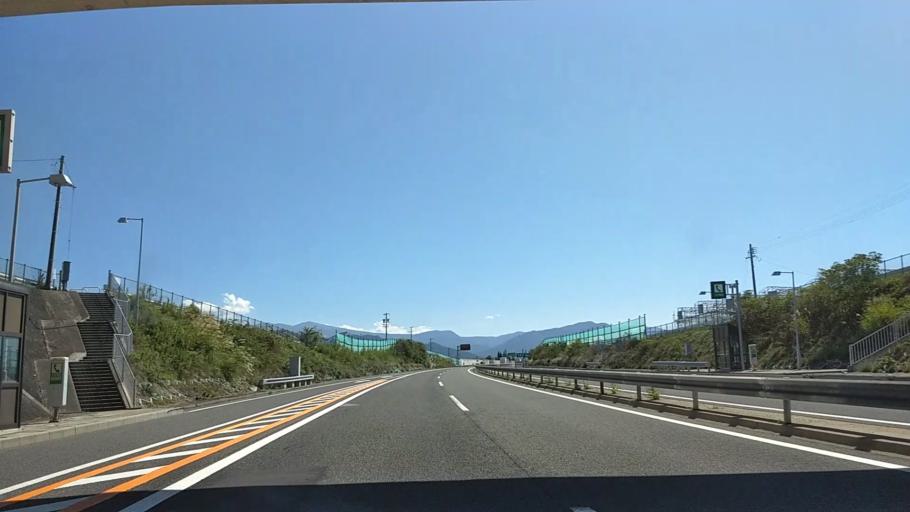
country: JP
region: Nagano
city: Nakano
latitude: 36.7372
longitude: 138.3177
